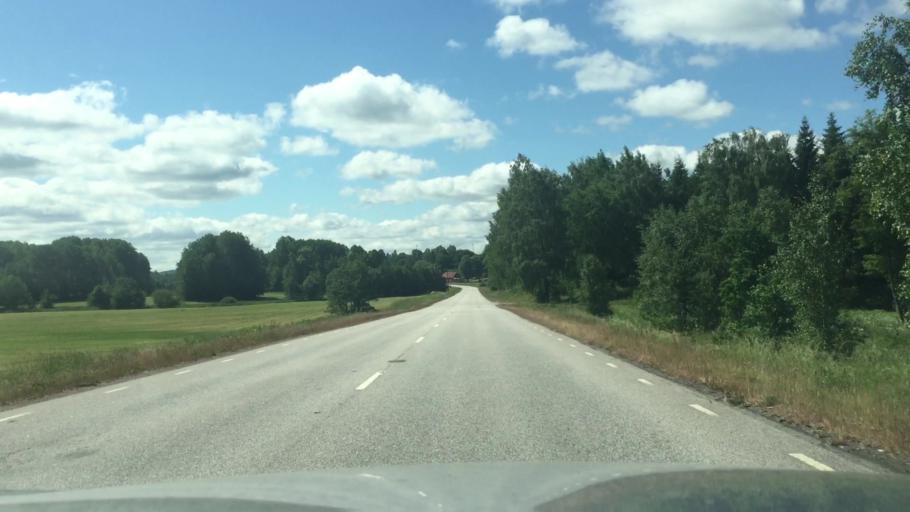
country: SE
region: Vaestra Goetaland
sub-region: Karlsborgs Kommun
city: Molltorp
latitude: 58.6351
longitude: 14.3928
